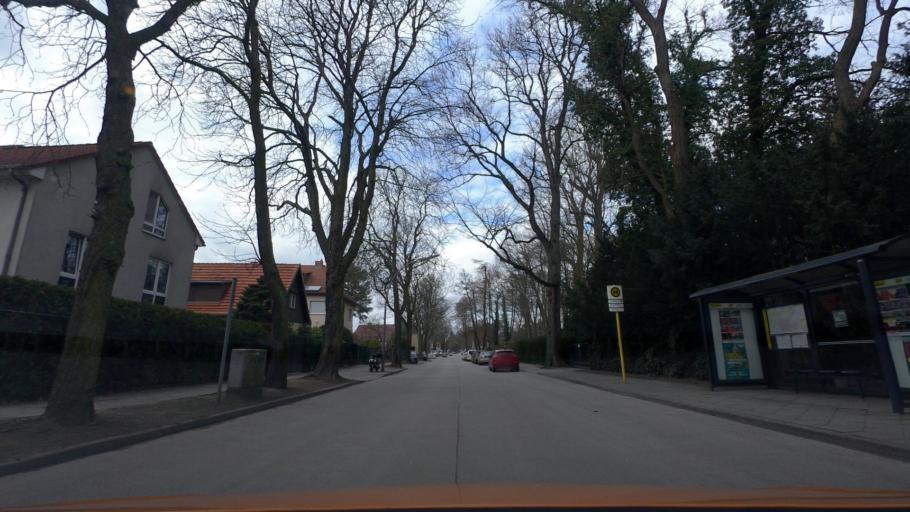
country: DE
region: Berlin
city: Konradshohe
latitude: 52.5983
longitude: 13.2156
